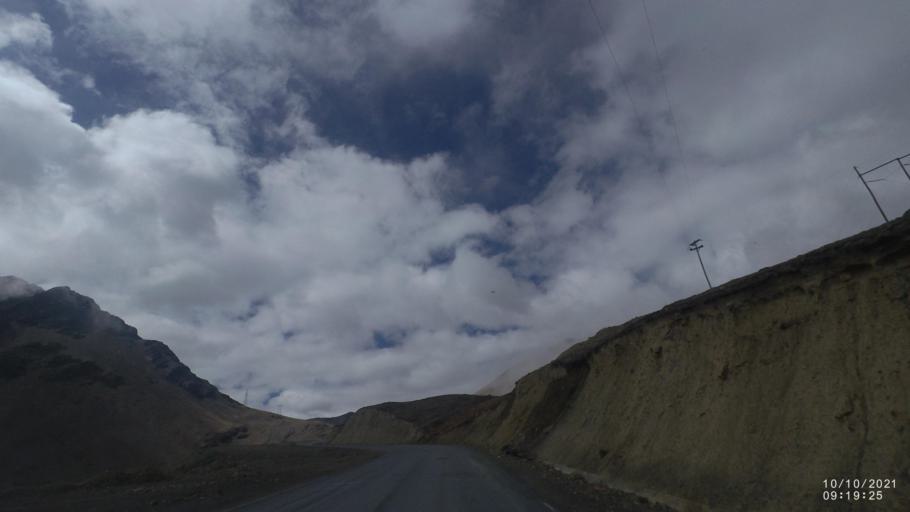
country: BO
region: La Paz
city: Quime
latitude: -17.0536
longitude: -67.2998
